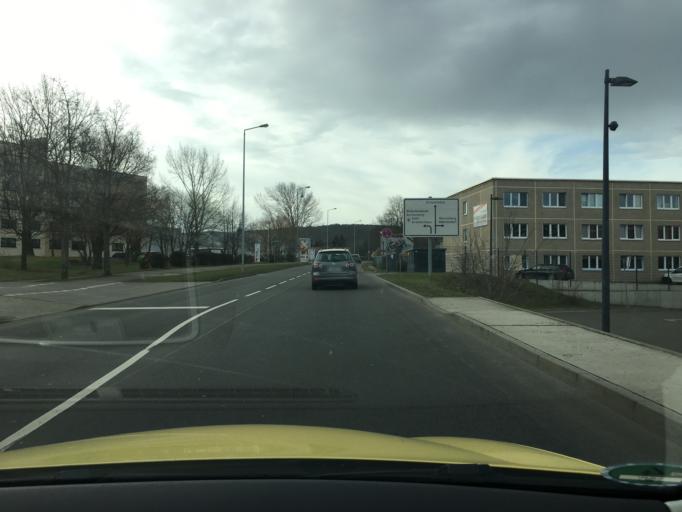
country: DE
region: Thuringia
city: Erfurt
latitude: 50.9522
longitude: 11.0824
